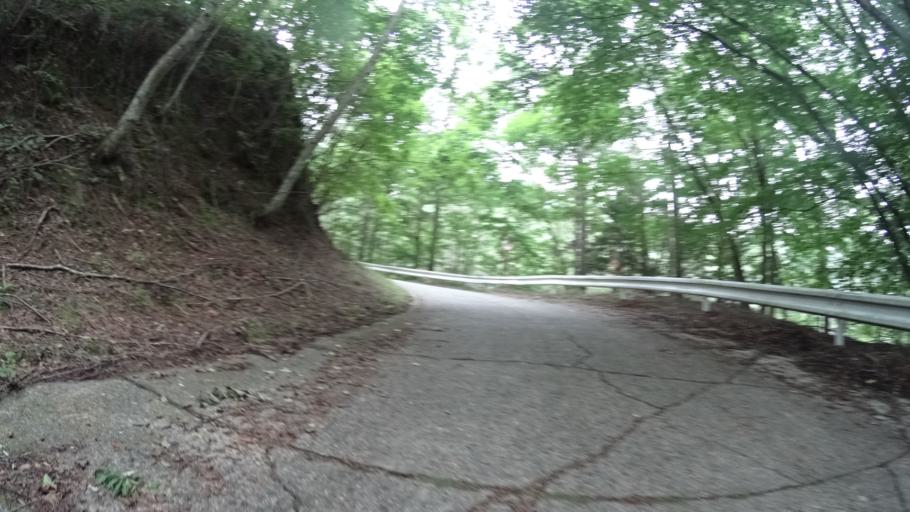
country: JP
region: Yamanashi
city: Kofu-shi
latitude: 35.8527
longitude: 138.5770
